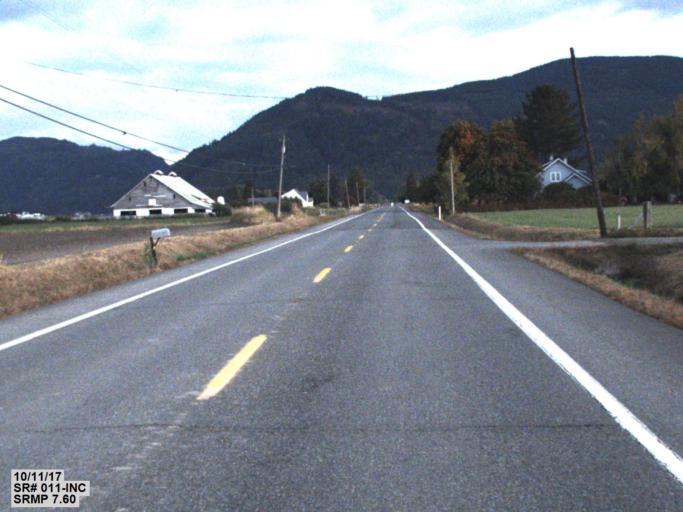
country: US
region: Washington
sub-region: Skagit County
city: Burlington
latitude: 48.5758
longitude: -122.4221
